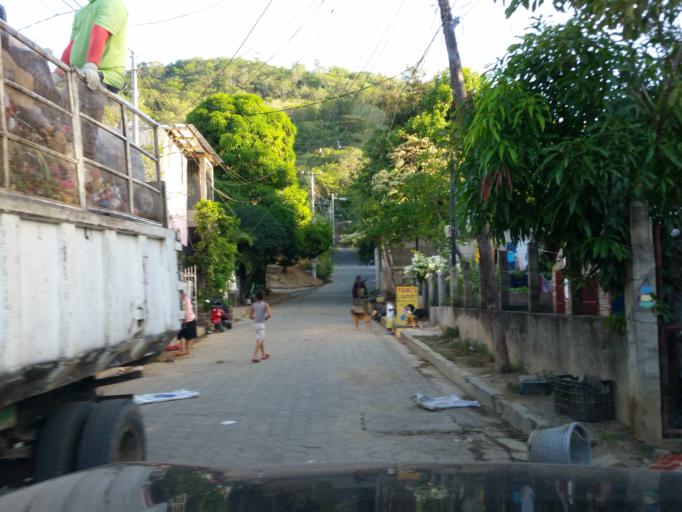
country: NI
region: Rivas
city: San Juan del Sur
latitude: 11.2507
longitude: -85.8689
